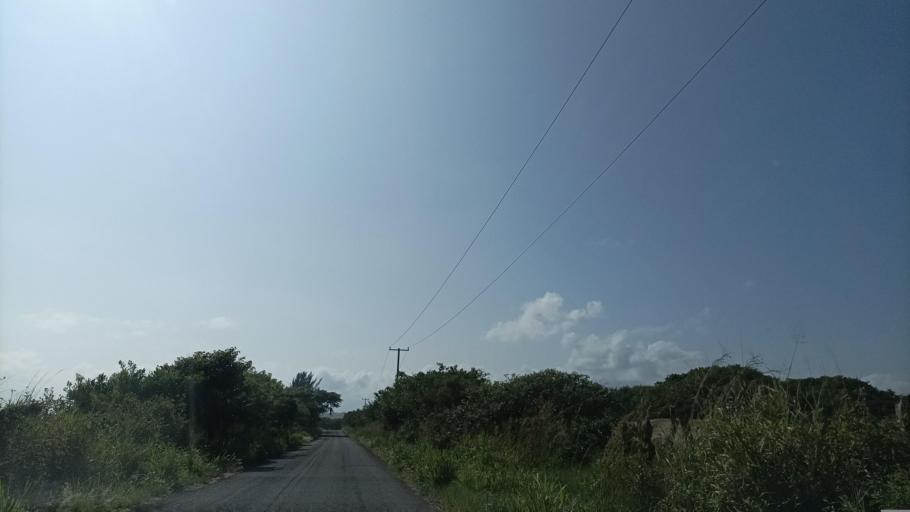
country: MX
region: Veracruz
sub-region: Pajapan
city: Pajapan
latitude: 18.2381
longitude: -94.6206
